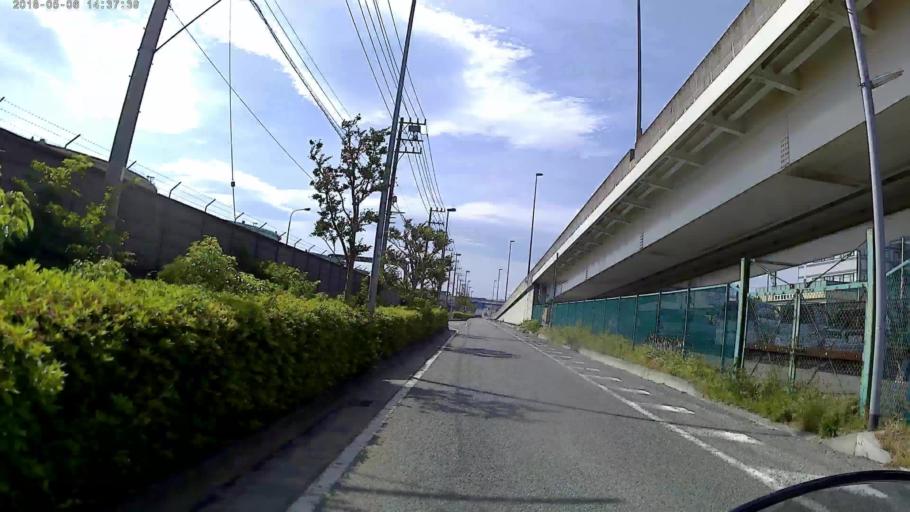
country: JP
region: Kanagawa
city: Yokohama
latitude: 35.4115
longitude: 139.6747
